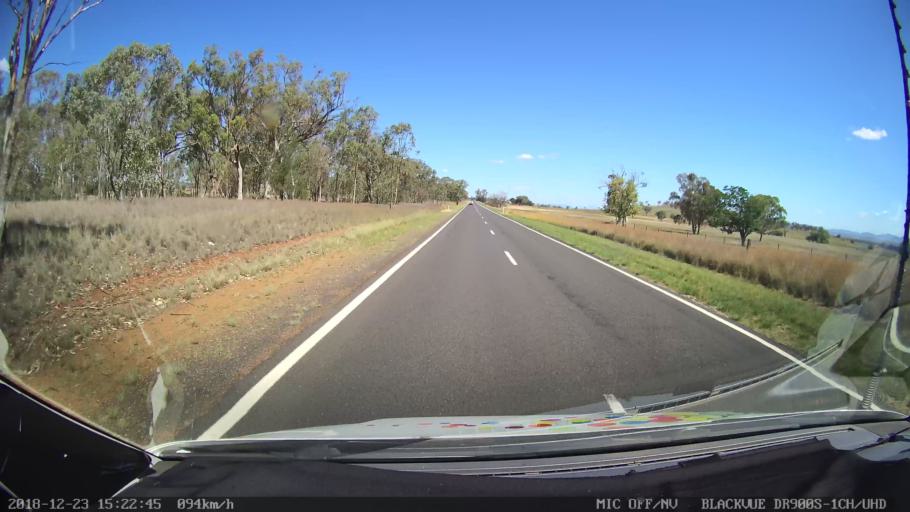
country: AU
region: New South Wales
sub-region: Tamworth Municipality
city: Manilla
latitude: -30.8721
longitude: 150.8078
